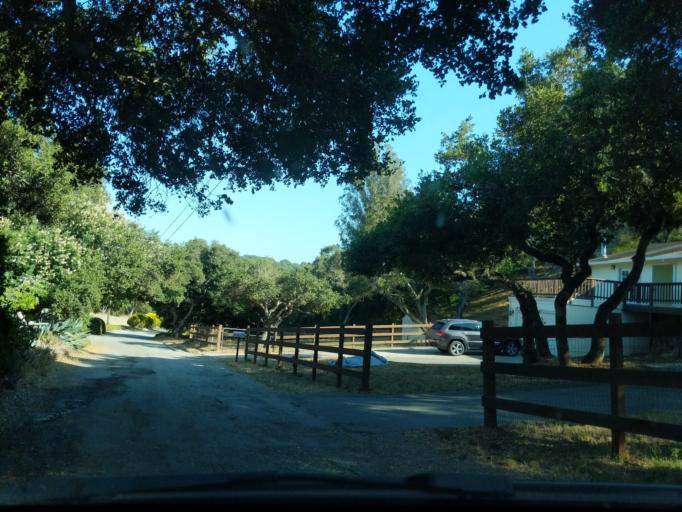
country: US
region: California
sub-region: Monterey County
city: Prunedale
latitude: 36.8029
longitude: -121.6446
